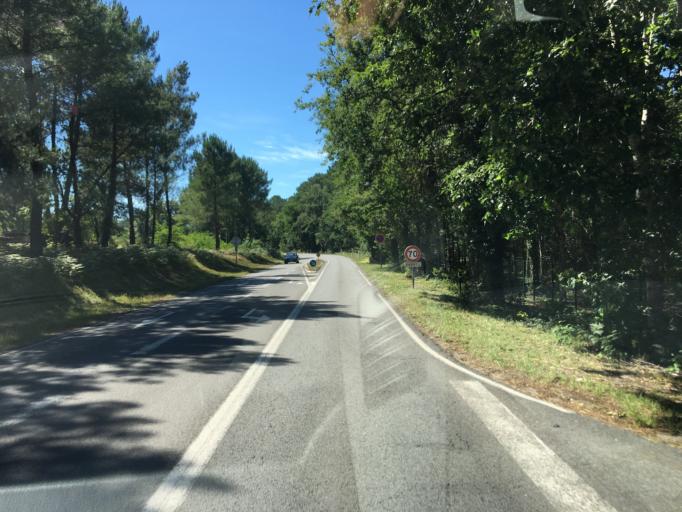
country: FR
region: Aquitaine
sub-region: Departement de la Gironde
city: Belin-Beliet
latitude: 44.4954
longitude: -0.6517
